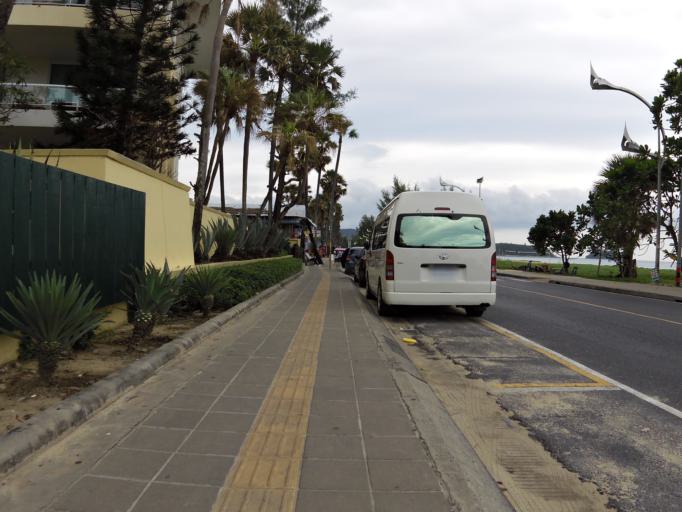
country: TH
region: Phuket
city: Ban Karon
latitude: 7.8455
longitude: 98.2939
